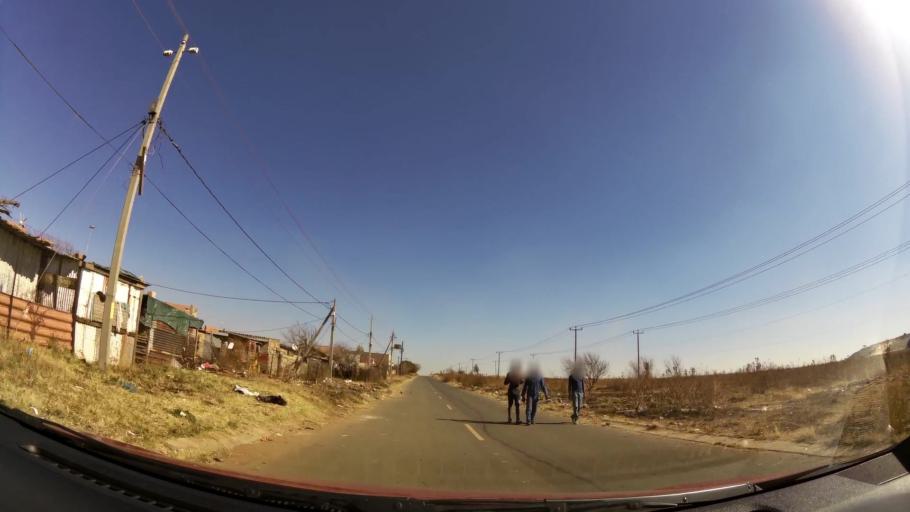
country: ZA
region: Gauteng
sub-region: City of Johannesburg Metropolitan Municipality
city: Soweto
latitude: -26.2158
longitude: 27.8382
